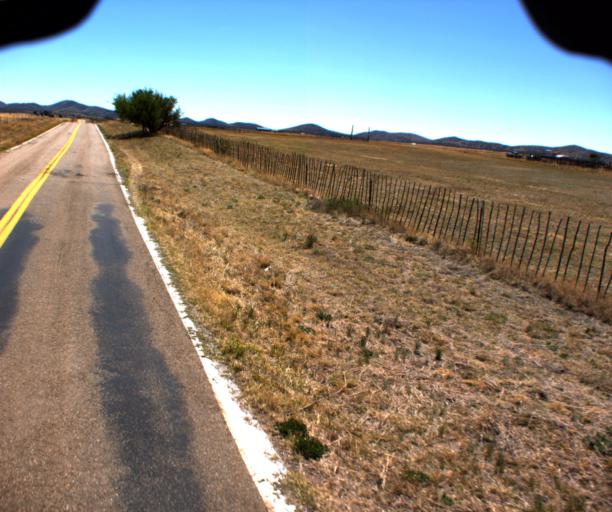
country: US
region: Arizona
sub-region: Cochise County
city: Huachuca City
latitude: 31.6174
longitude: -110.5871
